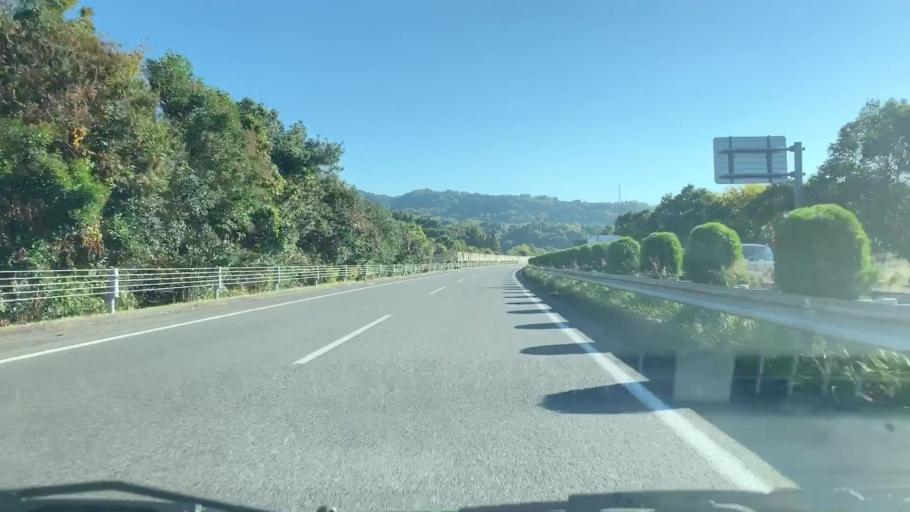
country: JP
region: Saga Prefecture
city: Takeocho-takeo
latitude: 33.2883
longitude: 130.1342
